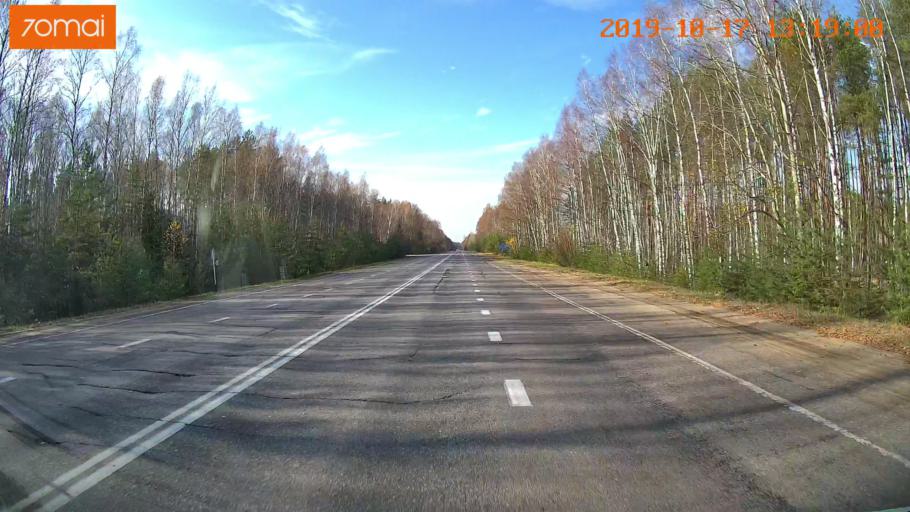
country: RU
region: Rjazan
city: Gus'-Zheleznyy
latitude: 55.0666
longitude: 41.0844
